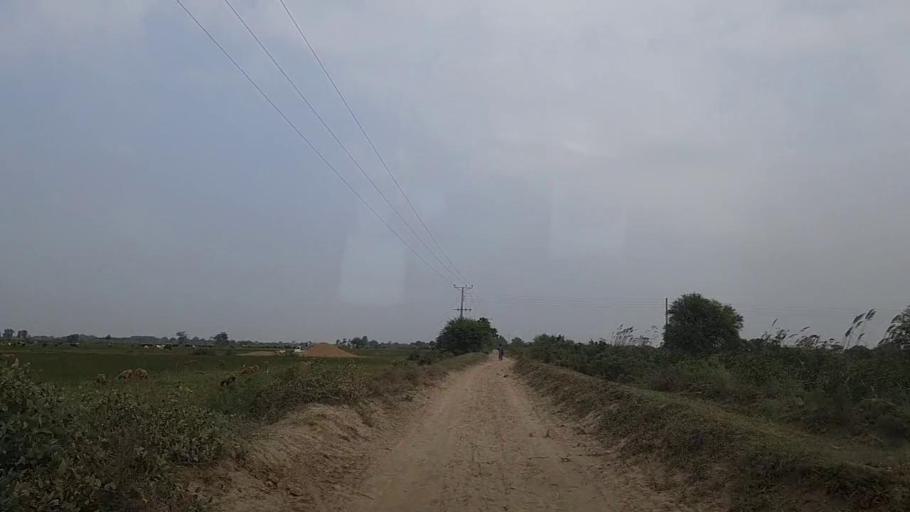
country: PK
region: Sindh
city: Mirpur Sakro
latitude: 24.6093
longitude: 67.7087
